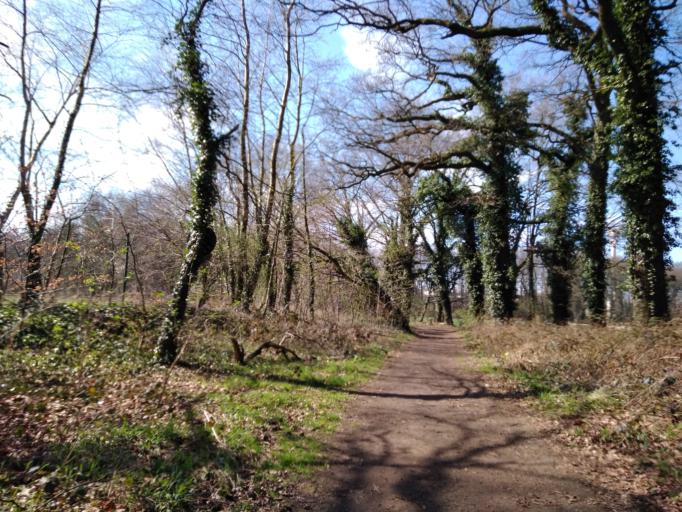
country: DE
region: North Rhine-Westphalia
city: Dorsten
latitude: 51.6219
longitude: 6.9815
